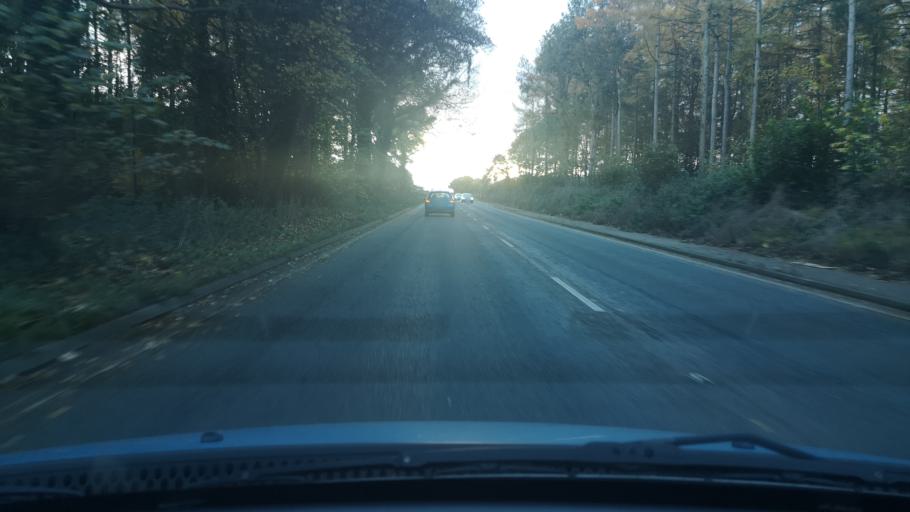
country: GB
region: England
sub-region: City and Borough of Wakefield
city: Horbury
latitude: 53.6322
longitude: -1.5610
